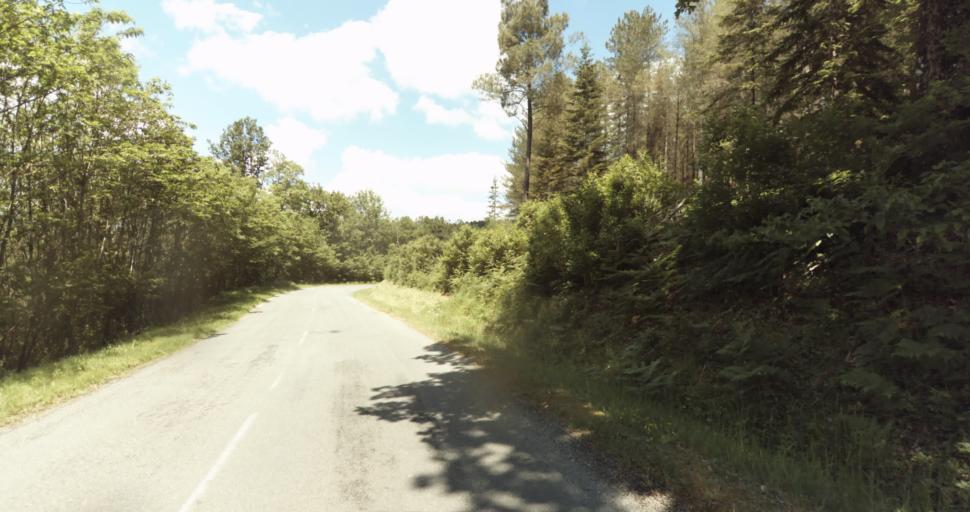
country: FR
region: Aquitaine
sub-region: Departement de la Dordogne
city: Beaumont-du-Perigord
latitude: 44.8113
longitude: 0.8572
